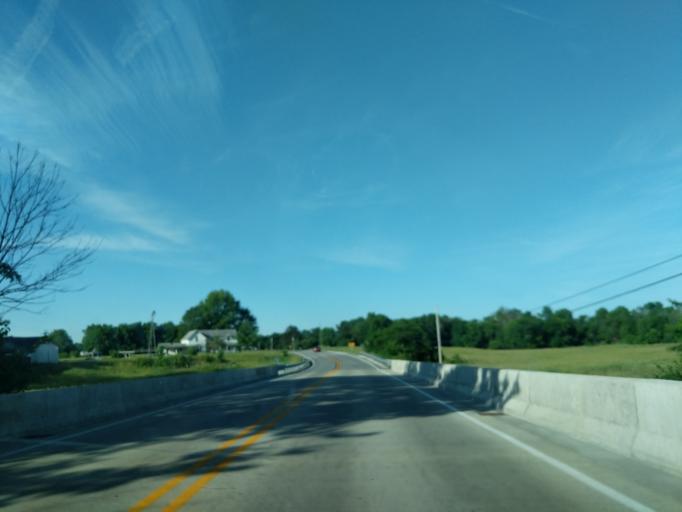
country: US
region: Indiana
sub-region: Madison County
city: Ingalls
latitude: 39.9562
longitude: -85.7627
